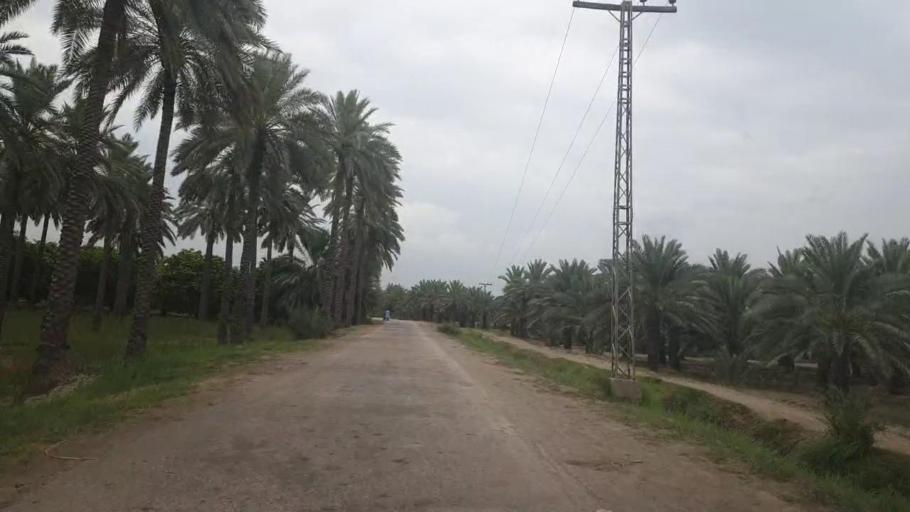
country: PK
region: Sindh
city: Khairpur
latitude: 27.5697
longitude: 68.7033
